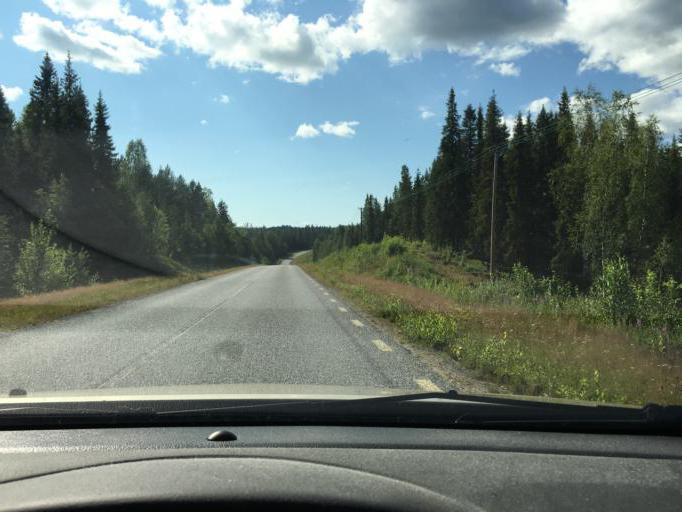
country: SE
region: Norrbotten
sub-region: Kalix Kommun
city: Toere
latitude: 66.0534
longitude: 22.5573
